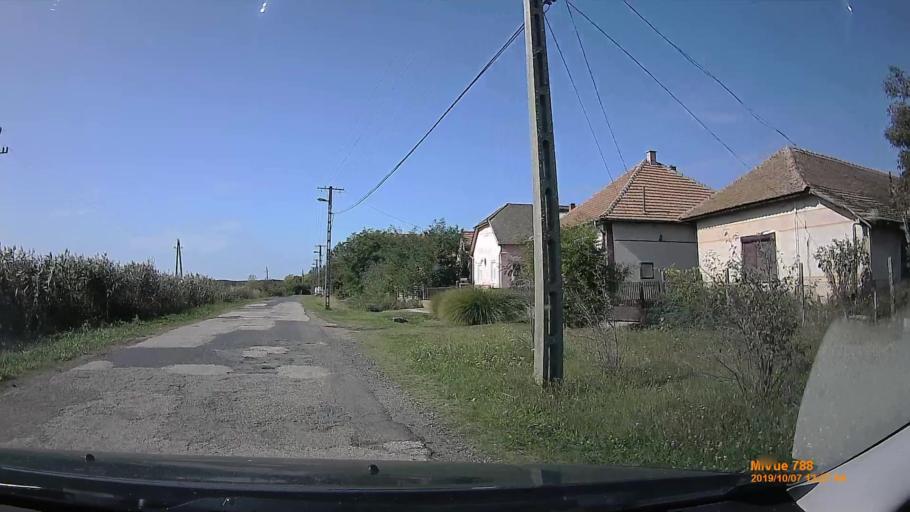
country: HU
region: Bacs-Kiskun
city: Tiszakecske
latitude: 46.8827
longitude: 20.1317
